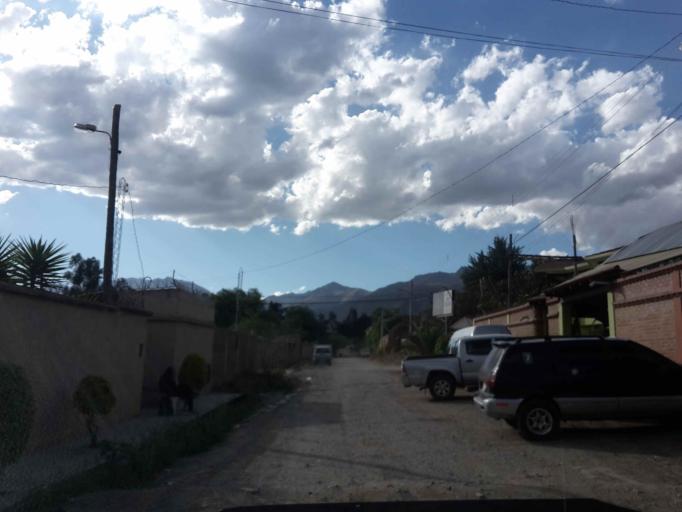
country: BO
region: Cochabamba
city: Cochabamba
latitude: -17.3488
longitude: -66.2026
